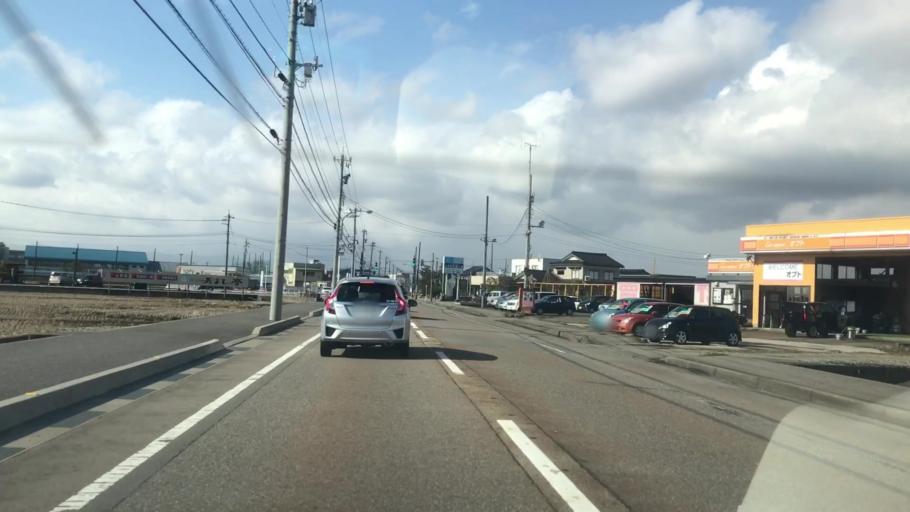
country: JP
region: Toyama
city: Takaoka
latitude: 36.7274
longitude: 137.0612
